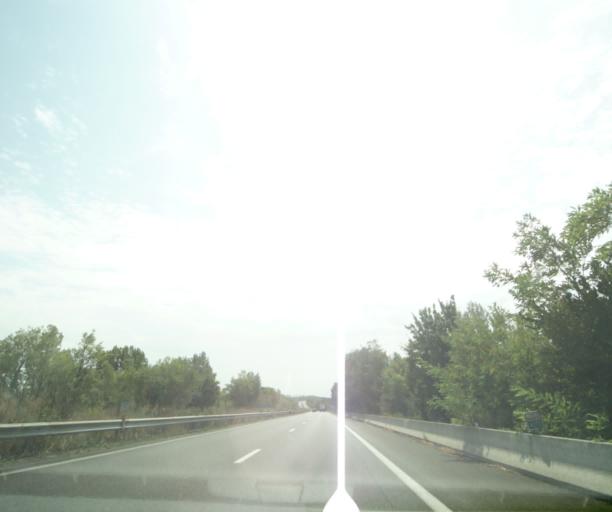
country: FR
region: Poitou-Charentes
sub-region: Departement de la Charente-Maritime
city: Saint-Savinien
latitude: 45.8505
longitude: -0.6239
